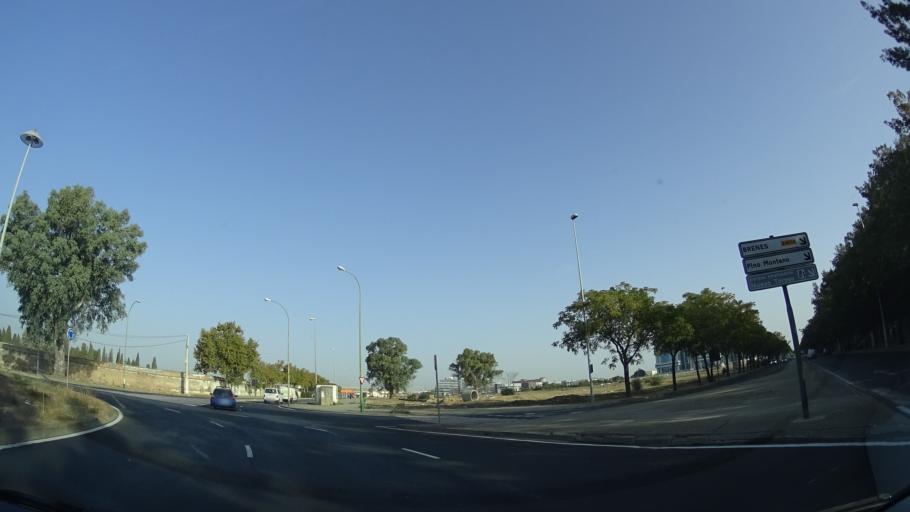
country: ES
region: Andalusia
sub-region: Provincia de Sevilla
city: Sevilla
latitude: 37.4206
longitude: -5.9765
